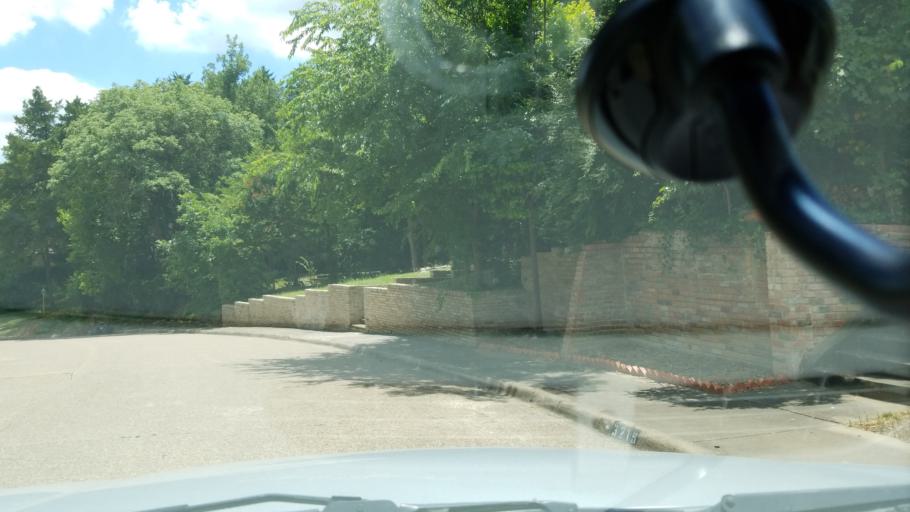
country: US
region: Texas
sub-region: Dallas County
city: Cockrell Hill
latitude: 32.7049
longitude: -96.8809
